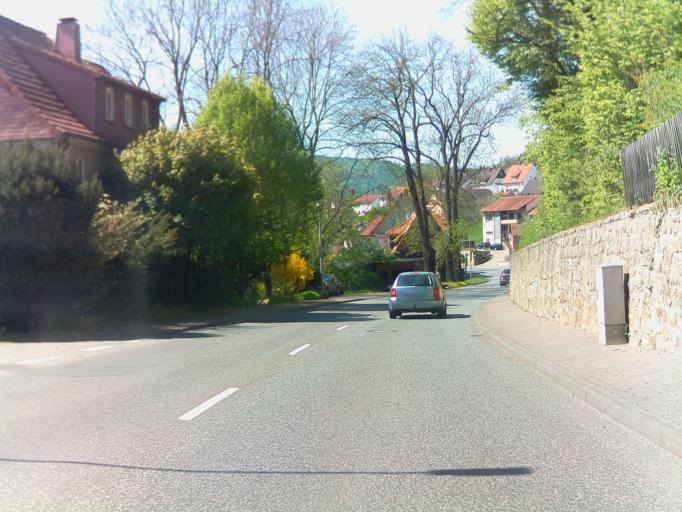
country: DE
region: Hesse
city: Grebenau
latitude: 50.7727
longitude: 9.5250
